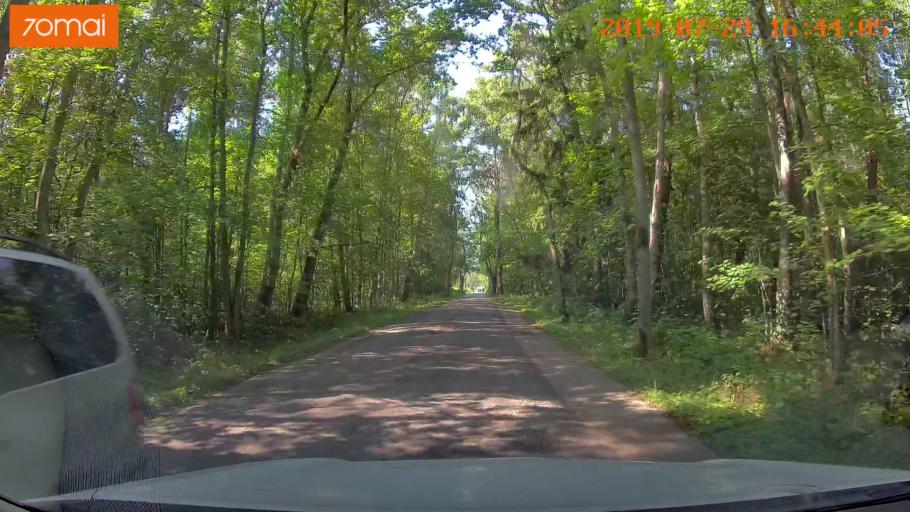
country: RU
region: Kaliningrad
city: Primorsk
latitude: 54.7527
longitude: 20.0898
